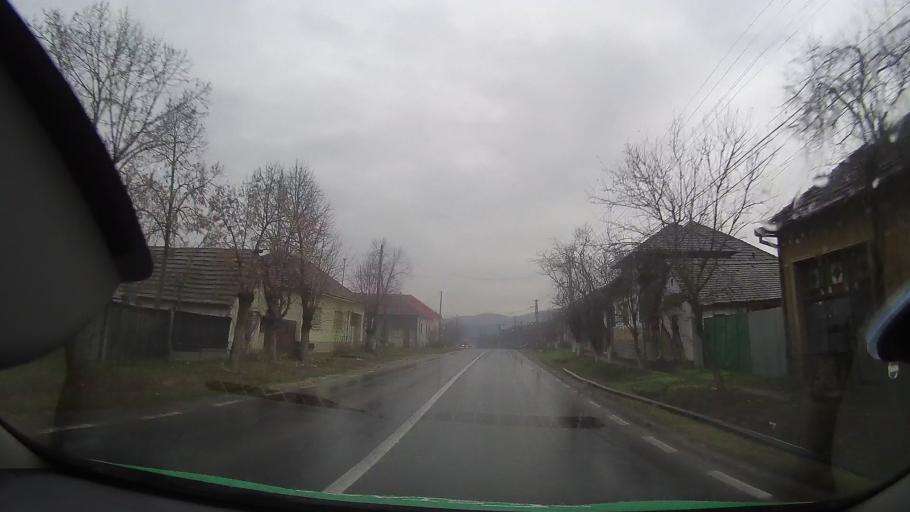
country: RO
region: Bihor
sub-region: Comuna Sambata
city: Sambata
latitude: 46.7991
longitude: 22.2031
